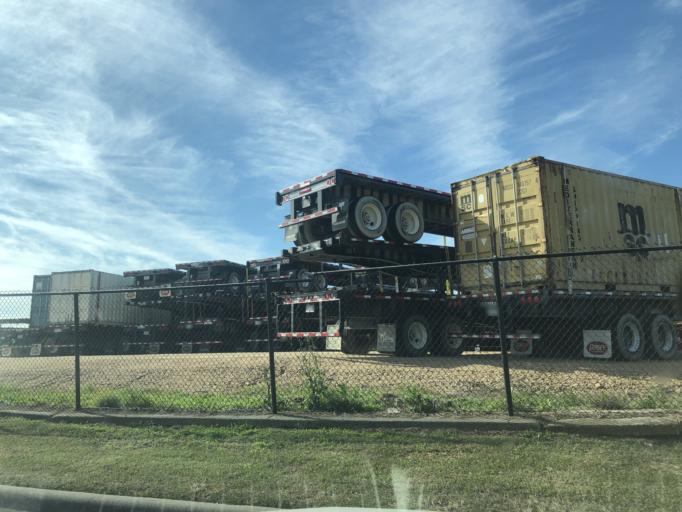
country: US
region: Texas
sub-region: Harris County
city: South Houston
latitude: 29.6629
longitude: -95.2539
